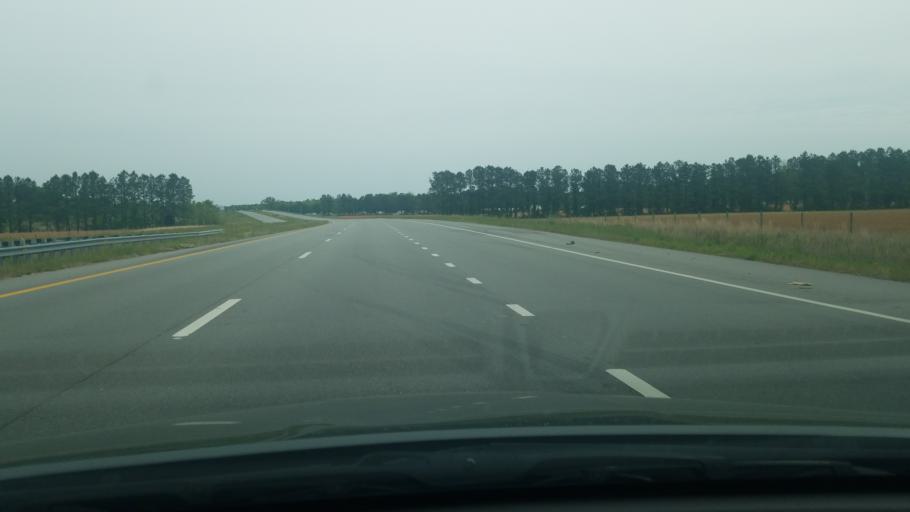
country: US
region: North Carolina
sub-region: Jones County
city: Maysville
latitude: 35.0035
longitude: -77.2307
